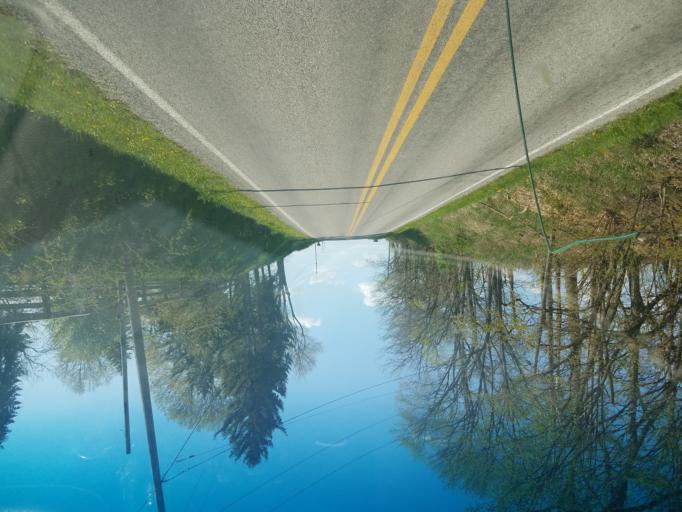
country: US
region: Ohio
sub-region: Wayne County
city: Creston
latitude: 40.9510
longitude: -81.9570
